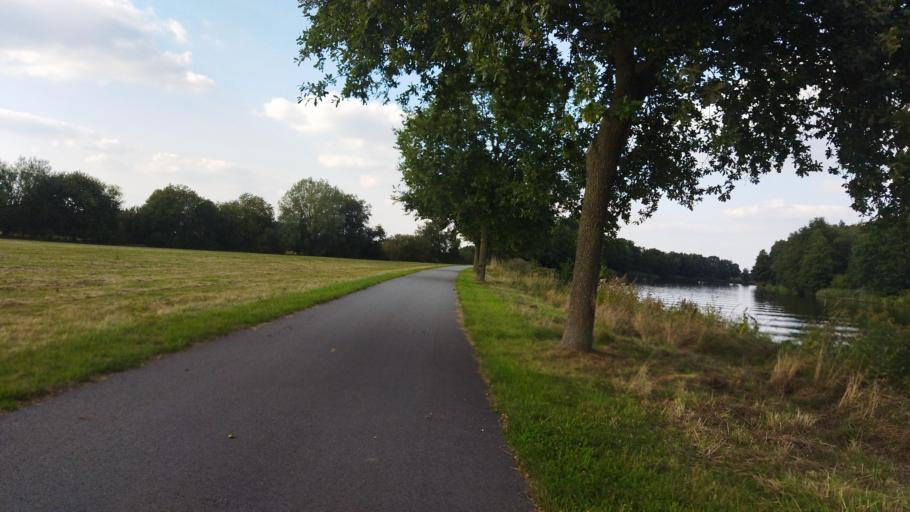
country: DE
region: Lower Saxony
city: Walchum
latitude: 52.9438
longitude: 7.2908
